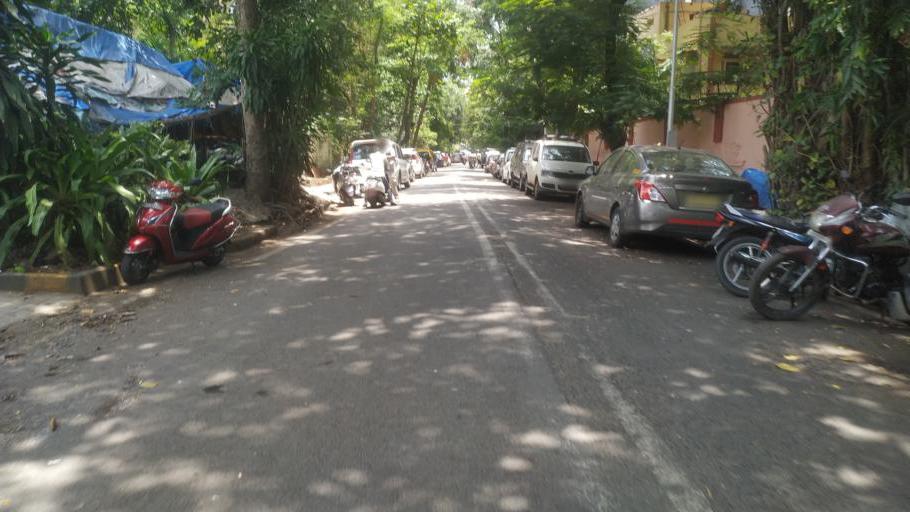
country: IN
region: Maharashtra
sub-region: Mumbai Suburban
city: Mumbai
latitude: 19.0162
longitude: 72.8266
